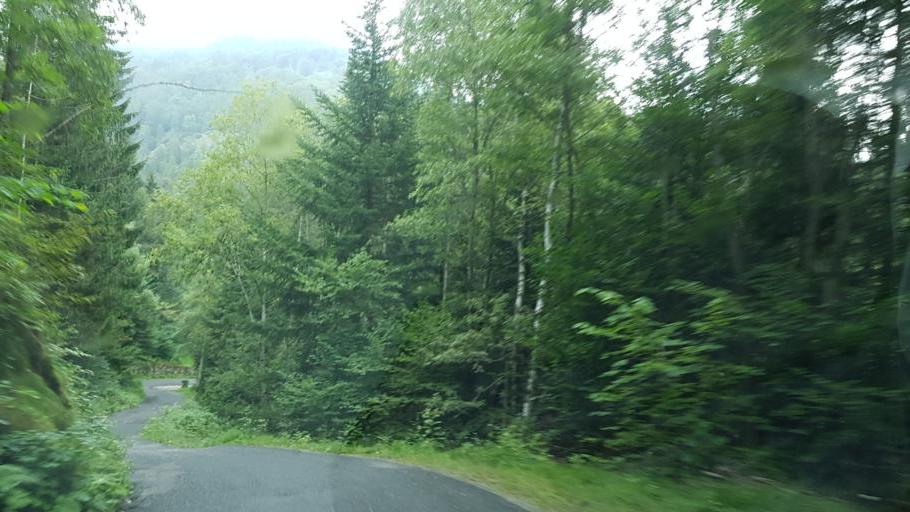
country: IT
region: Piedmont
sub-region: Provincia di Cuneo
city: Sampeyre
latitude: 44.5752
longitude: 7.1657
